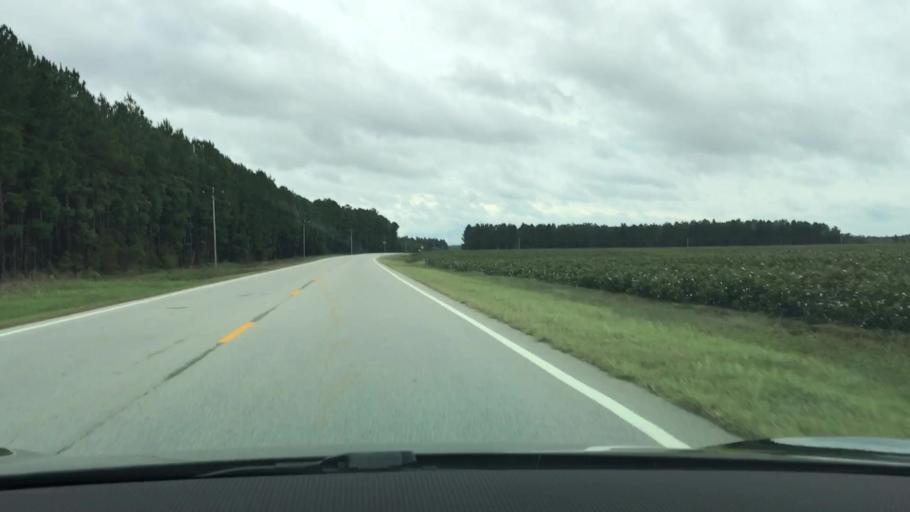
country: US
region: Georgia
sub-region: Glascock County
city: Gibson
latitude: 33.2872
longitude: -82.5074
